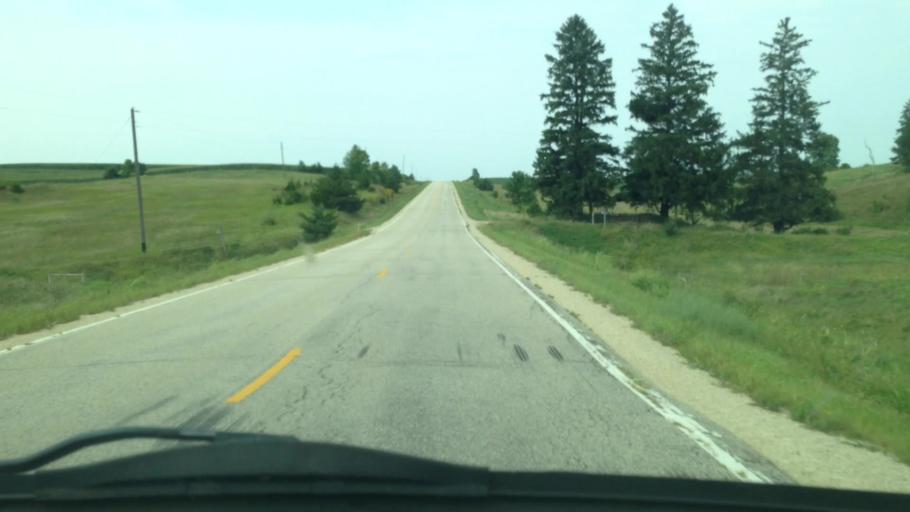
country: US
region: Minnesota
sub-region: Winona County
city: Saint Charles
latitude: 43.8518
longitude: -91.9594
